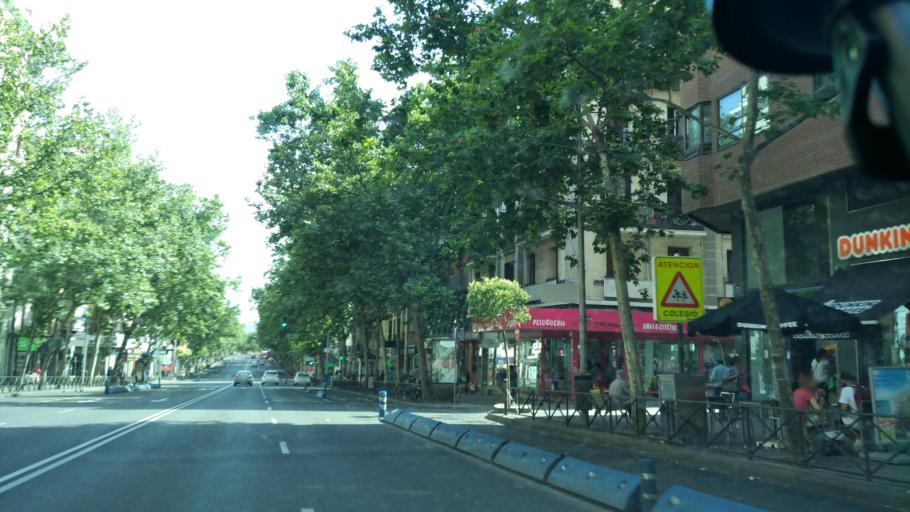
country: ES
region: Madrid
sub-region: Provincia de Madrid
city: Chamberi
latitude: 40.4514
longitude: -3.7033
